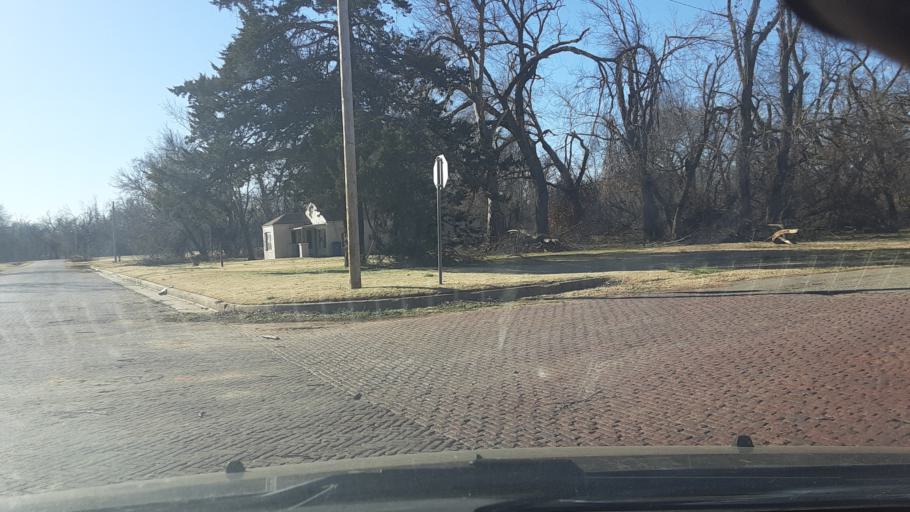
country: US
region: Oklahoma
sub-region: Logan County
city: Guthrie
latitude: 35.8739
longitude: -97.4276
